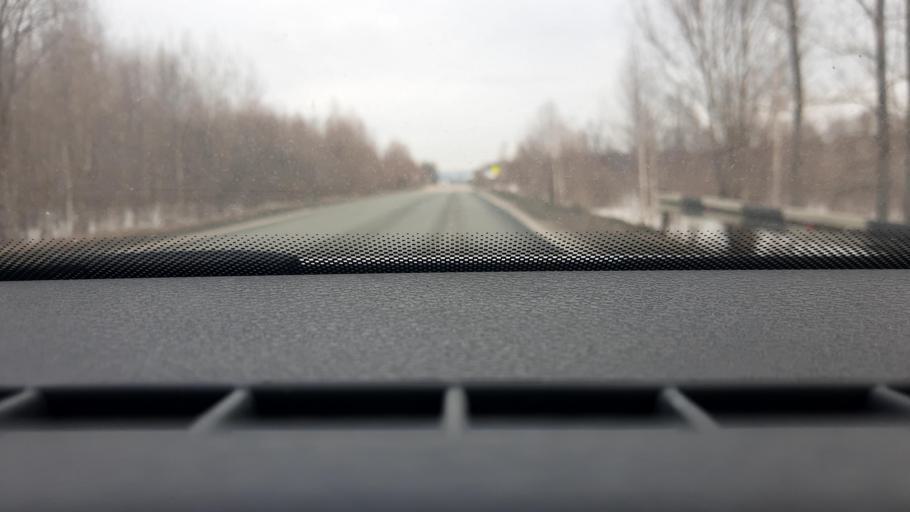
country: RU
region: Chelyabinsk
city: Asha
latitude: 54.9264
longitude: 57.2891
